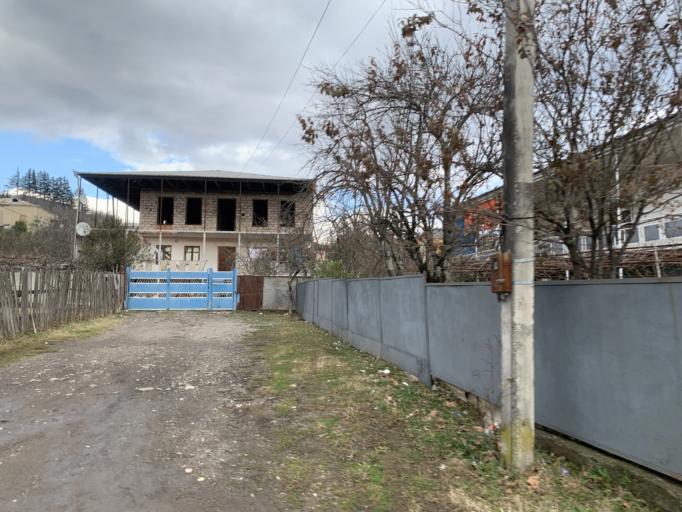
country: GE
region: Imereti
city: Tsqaltubo
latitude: 42.3309
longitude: 42.5968
